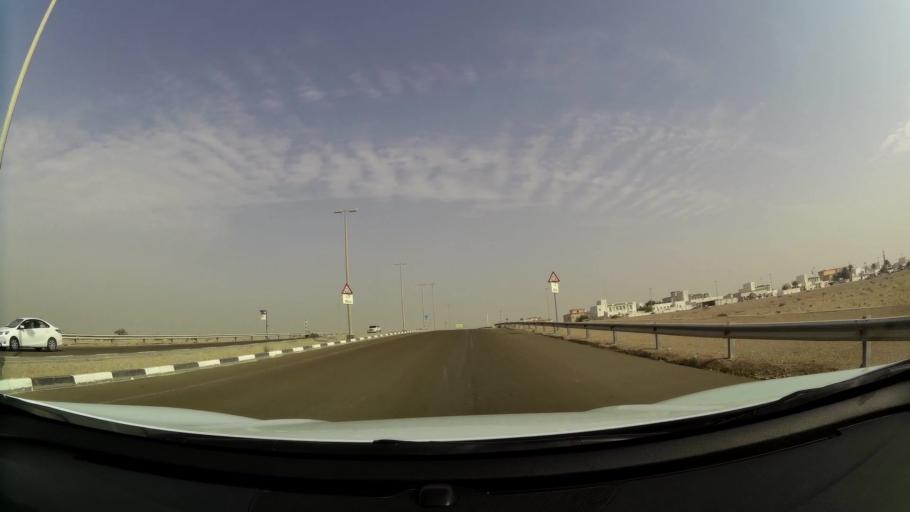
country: AE
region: Abu Dhabi
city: Abu Dhabi
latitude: 24.2742
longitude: 54.6841
